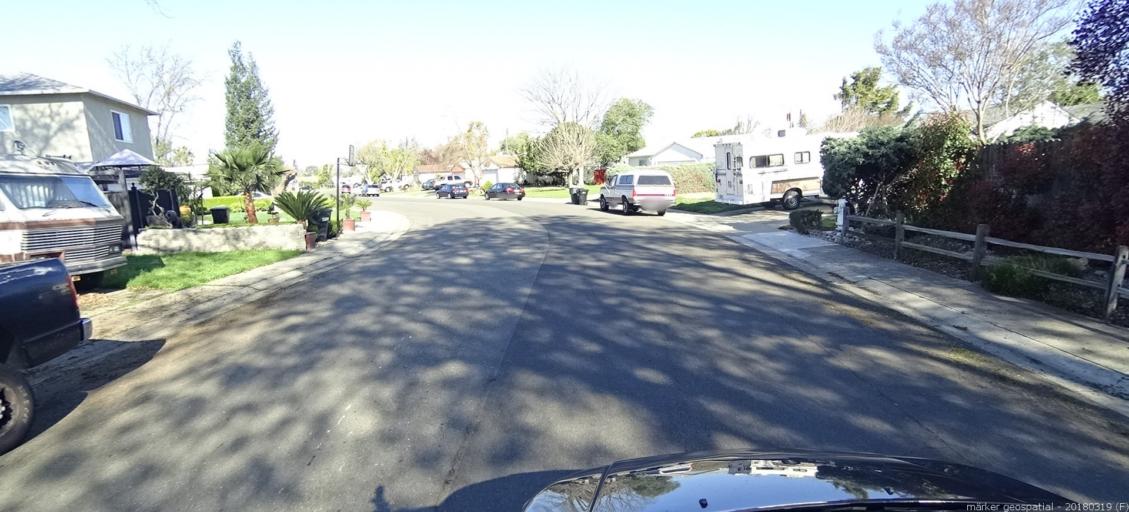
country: US
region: California
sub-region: Sacramento County
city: Parkway
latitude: 38.4887
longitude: -121.4513
